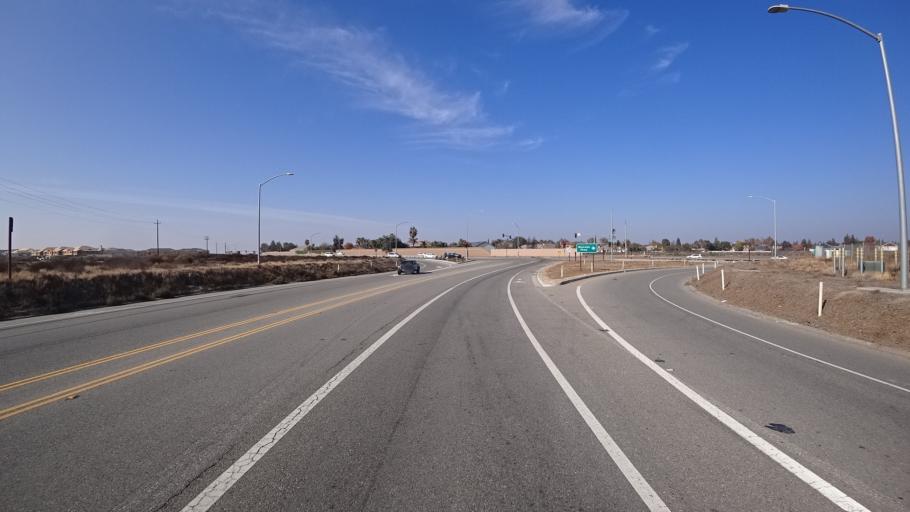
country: US
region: California
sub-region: Kern County
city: Rosedale
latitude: 35.3547
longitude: -119.1747
